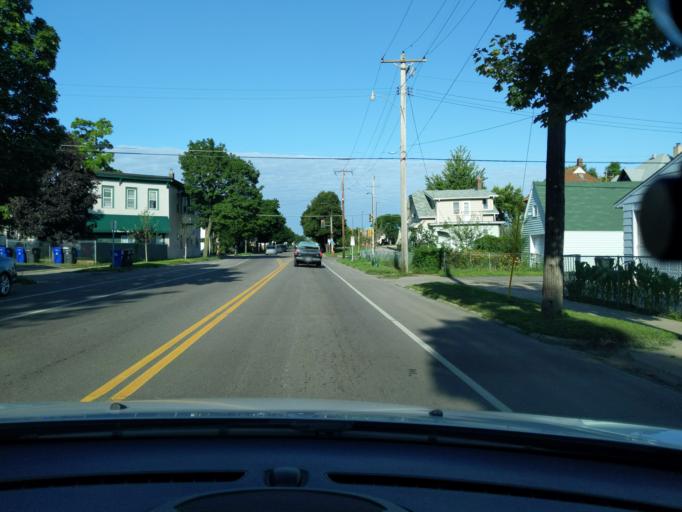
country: US
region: Minnesota
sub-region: Ramsey County
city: Saint Paul
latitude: 44.9630
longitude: -93.1151
